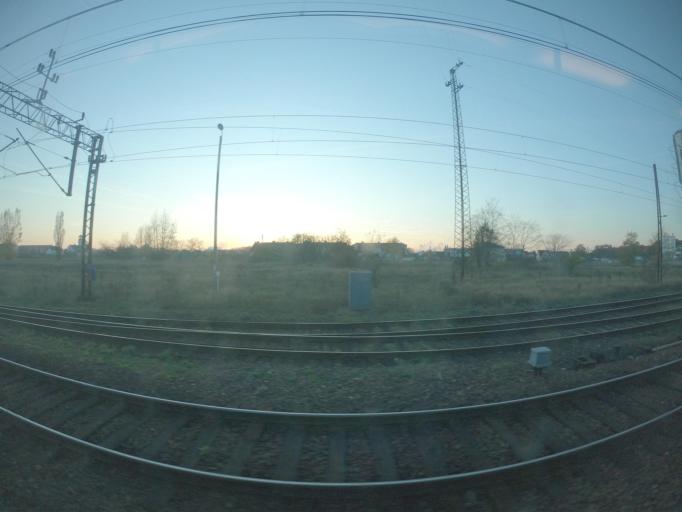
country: PL
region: Lubusz
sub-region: Powiat gorzowski
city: Kostrzyn nad Odra
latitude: 52.6013
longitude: 14.6467
